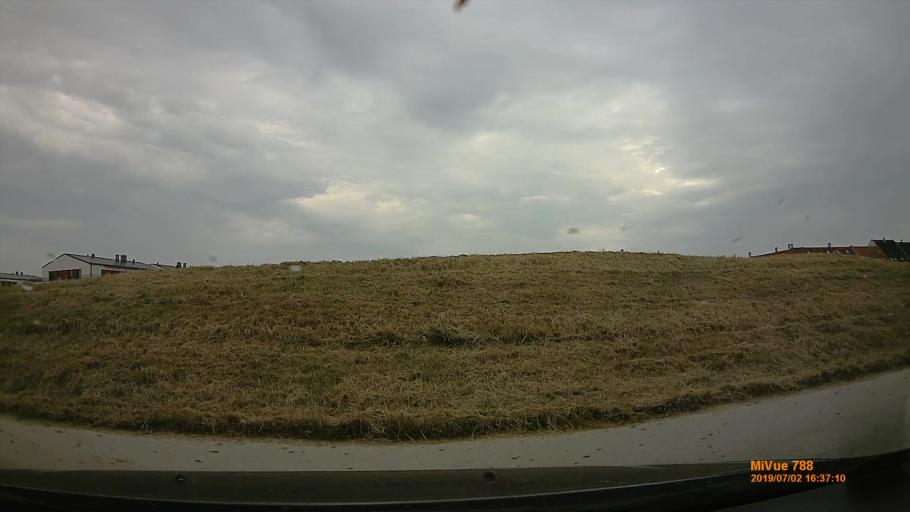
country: HU
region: Gyor-Moson-Sopron
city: Mosonmagyarovar
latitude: 47.8863
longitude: 17.2661
